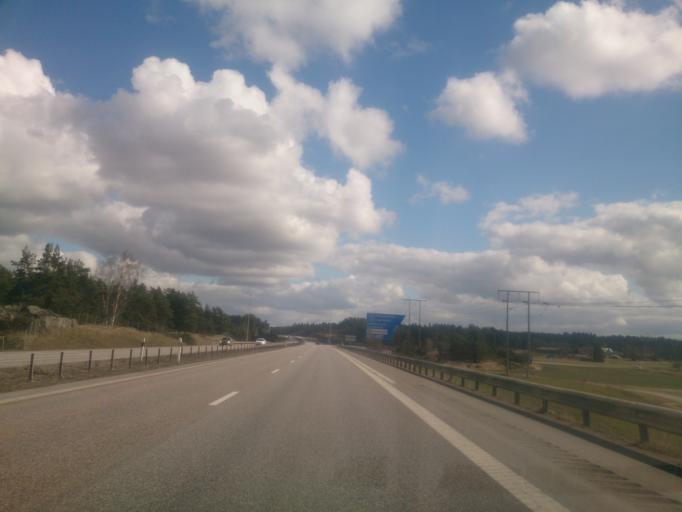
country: SE
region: OEstergoetland
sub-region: Norrkopings Kommun
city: Kimstad
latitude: 58.4883
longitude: 15.9390
